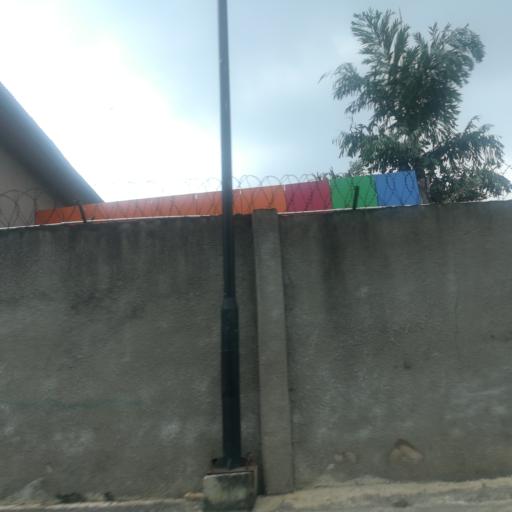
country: NG
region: Lagos
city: Ojota
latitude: 6.5840
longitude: 3.3841
